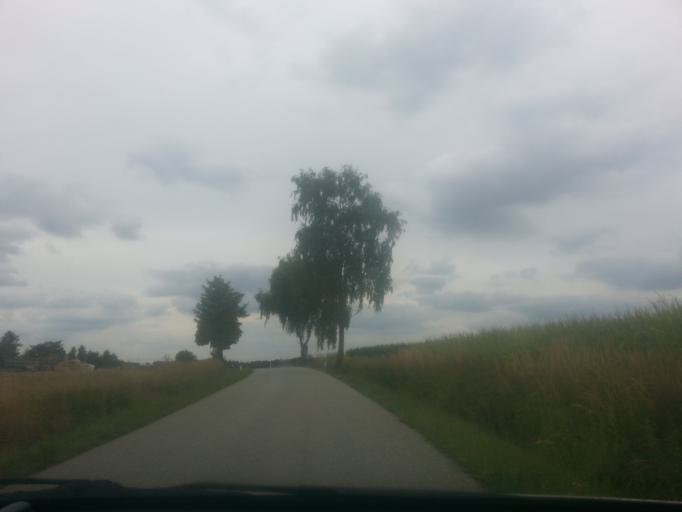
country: DE
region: Bavaria
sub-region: Lower Bavaria
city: Pfeffenhausen
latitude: 48.6712
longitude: 11.9119
